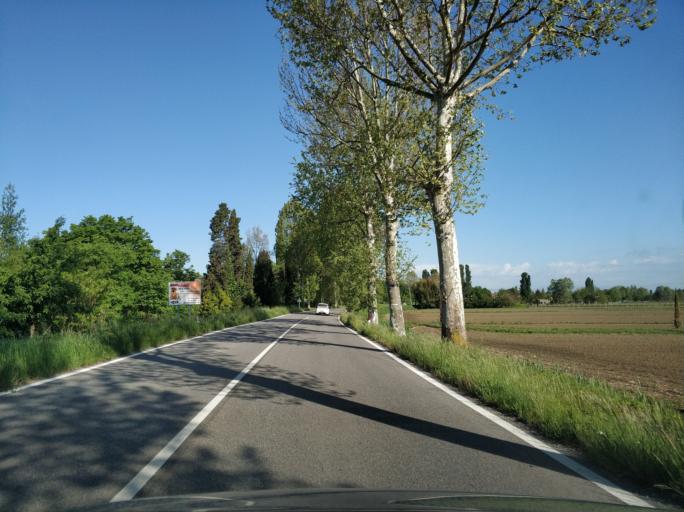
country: IT
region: Friuli Venezia Giulia
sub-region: Provincia di Udine
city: Terzo d'Aquileia
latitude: 45.8033
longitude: 13.3460
